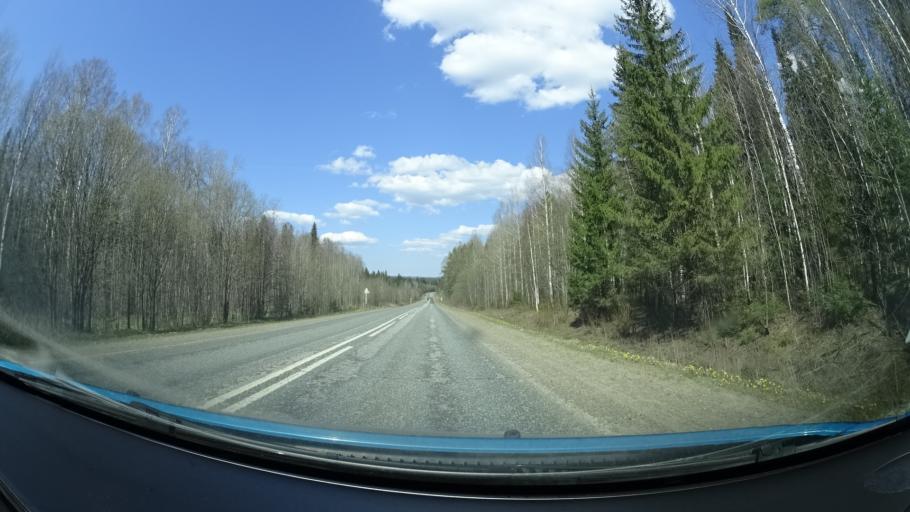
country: RU
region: Perm
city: Yugo-Kamskiy
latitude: 57.5197
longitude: 55.6854
